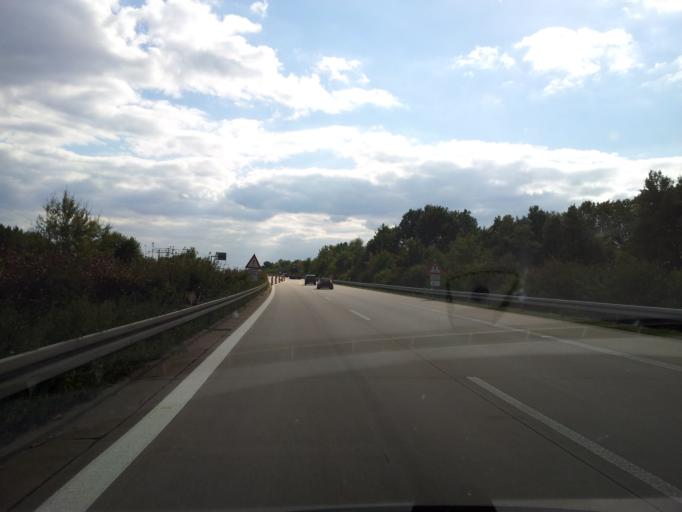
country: DE
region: Brandenburg
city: Schipkau
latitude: 51.5258
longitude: 13.9051
